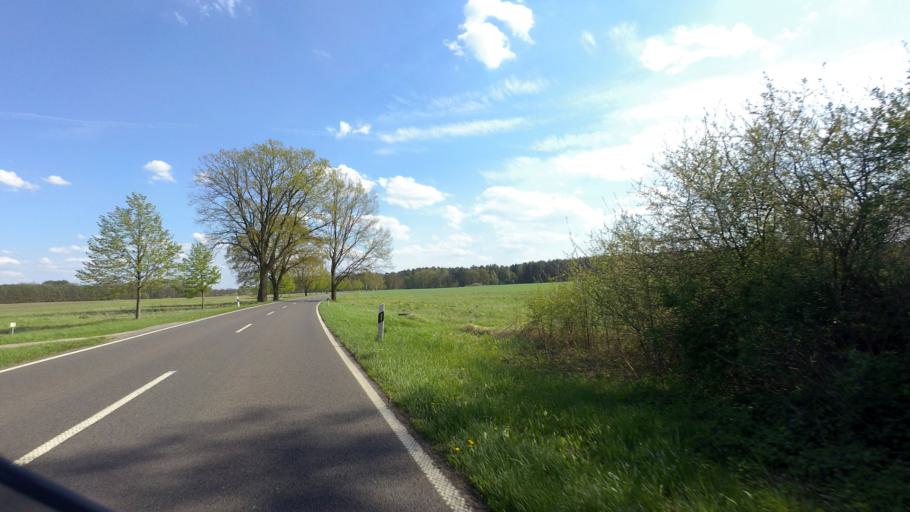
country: DE
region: Brandenburg
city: Templin
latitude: 53.0630
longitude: 13.5187
